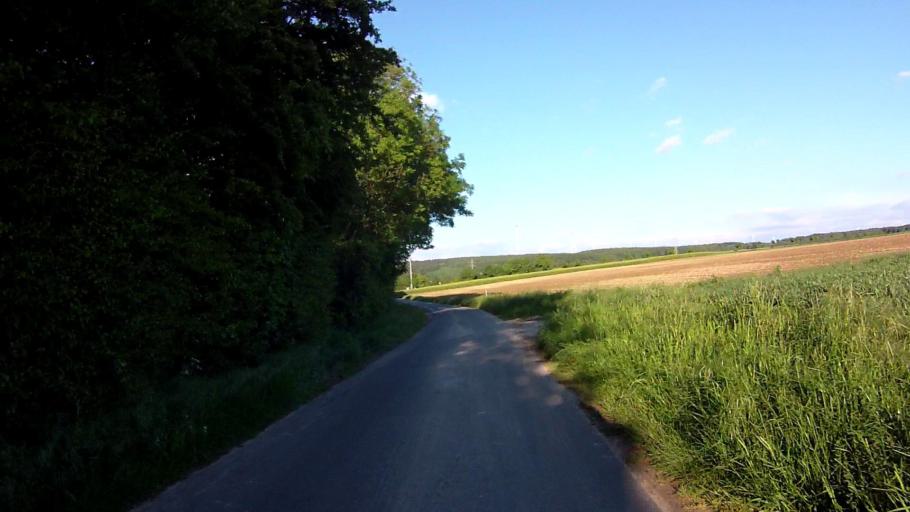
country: DE
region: North Rhine-Westphalia
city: Bad Lippspringe
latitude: 51.7413
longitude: 8.8467
